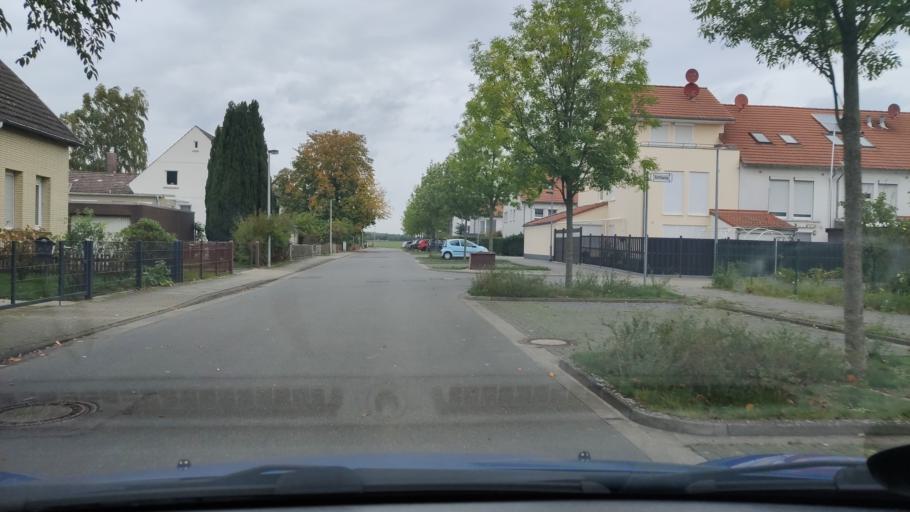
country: DE
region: Lower Saxony
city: Garbsen-Mitte
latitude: 52.4302
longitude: 9.6532
